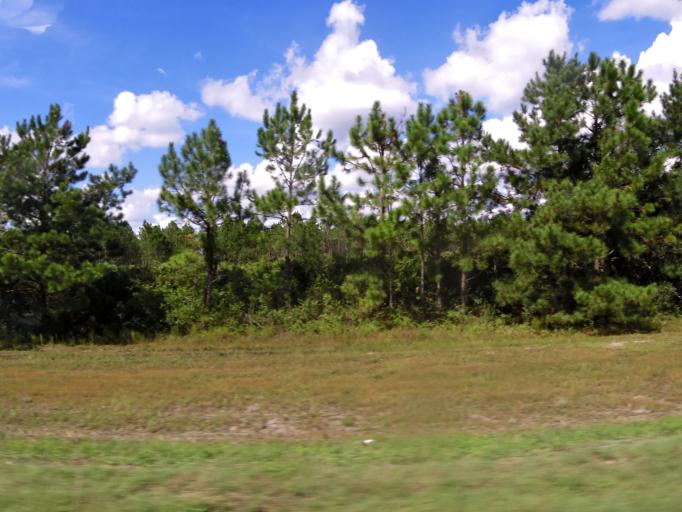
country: US
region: Georgia
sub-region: Clinch County
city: Homerville
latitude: 30.6807
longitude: -82.5964
